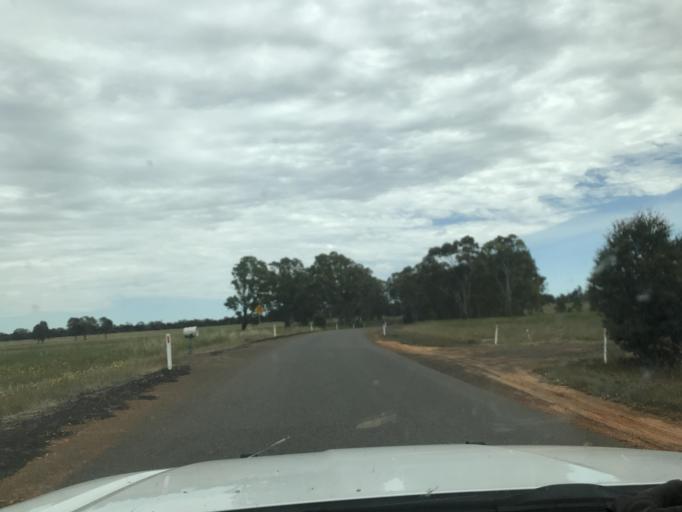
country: AU
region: Victoria
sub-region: Horsham
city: Horsham
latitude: -36.9764
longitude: 141.5233
